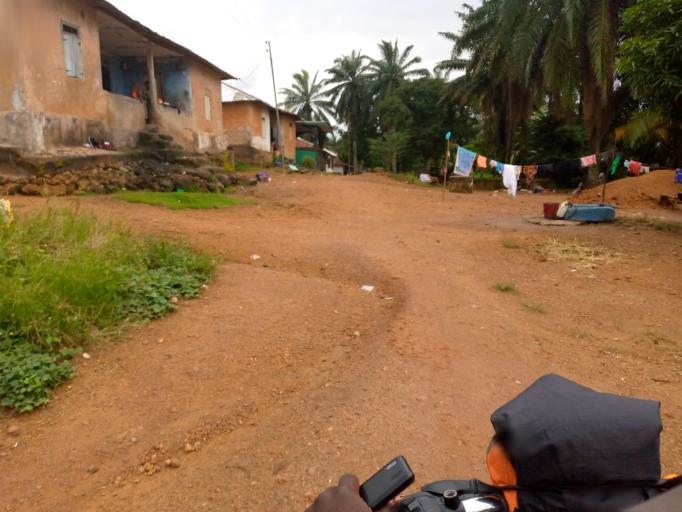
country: SL
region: Eastern Province
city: Kenema
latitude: 7.8709
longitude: -11.1864
